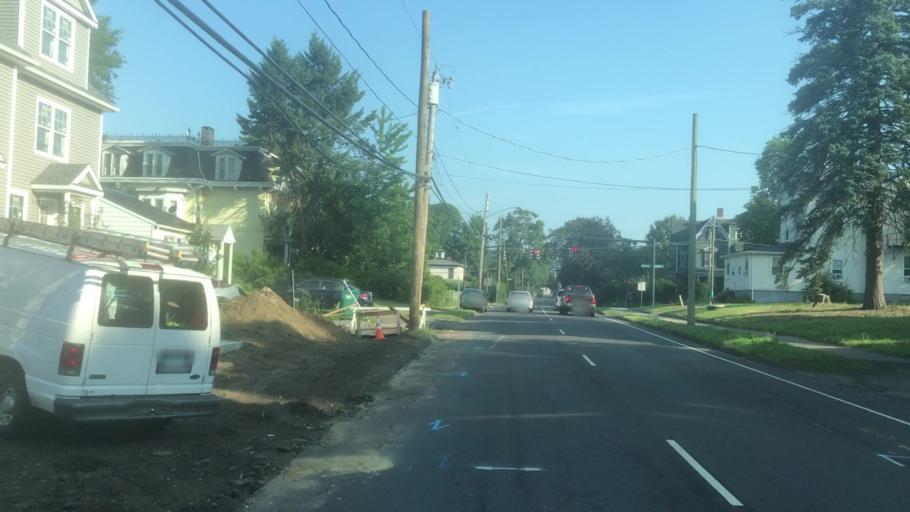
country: US
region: Connecticut
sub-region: Fairfield County
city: Danbury
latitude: 41.3992
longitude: -73.4522
